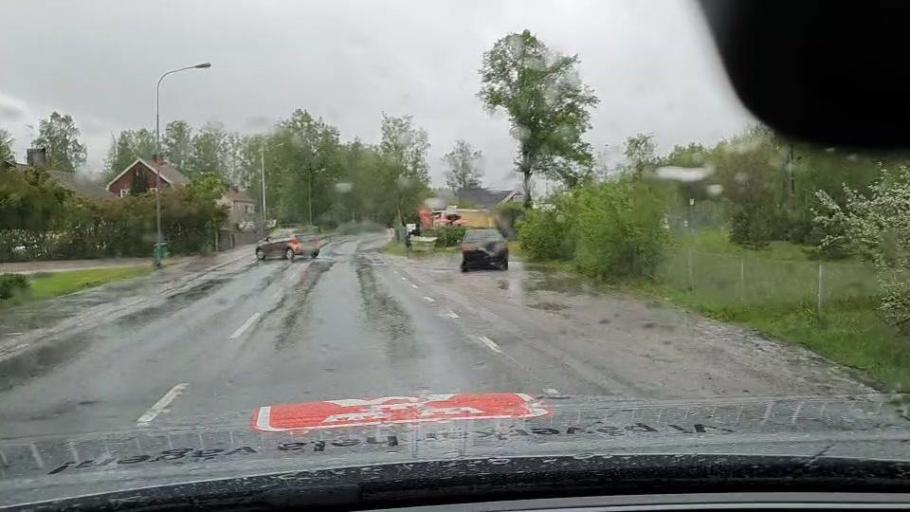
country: SE
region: Soedermanland
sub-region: Eskilstuna Kommun
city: Skogstorp
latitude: 59.2930
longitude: 16.4582
